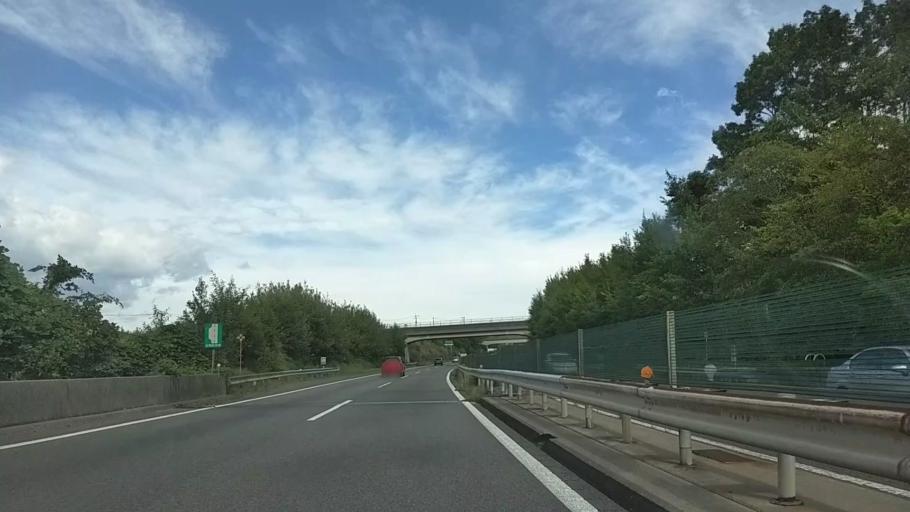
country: JP
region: Yamanashi
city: Nirasaki
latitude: 35.7039
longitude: 138.4767
